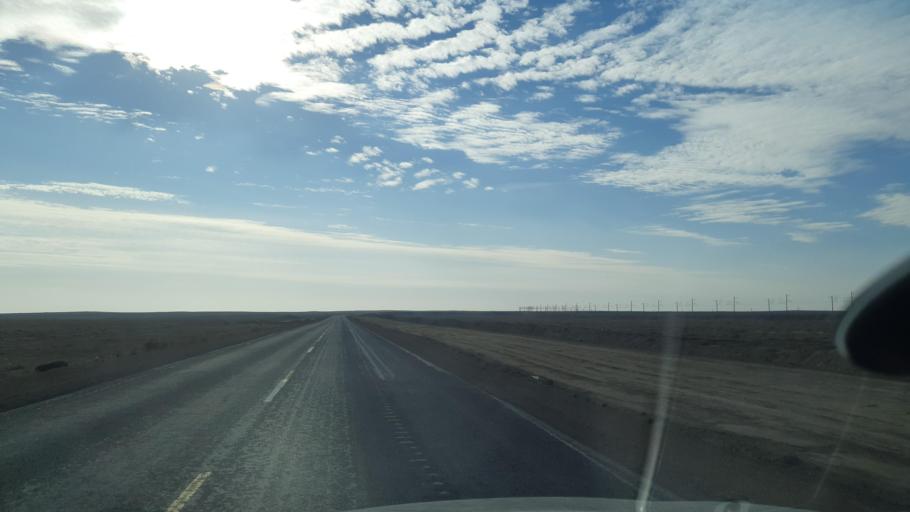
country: KZ
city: Priozersk
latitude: 45.9069
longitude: 73.5137
